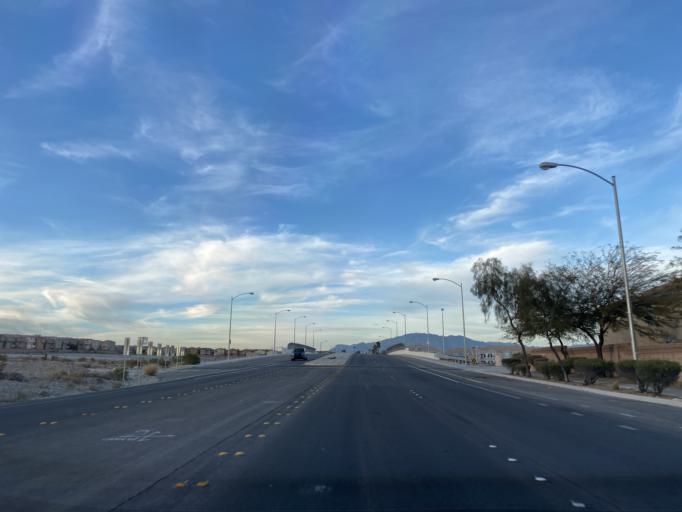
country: US
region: Nevada
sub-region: Clark County
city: Summerlin South
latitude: 36.2786
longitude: -115.2969
